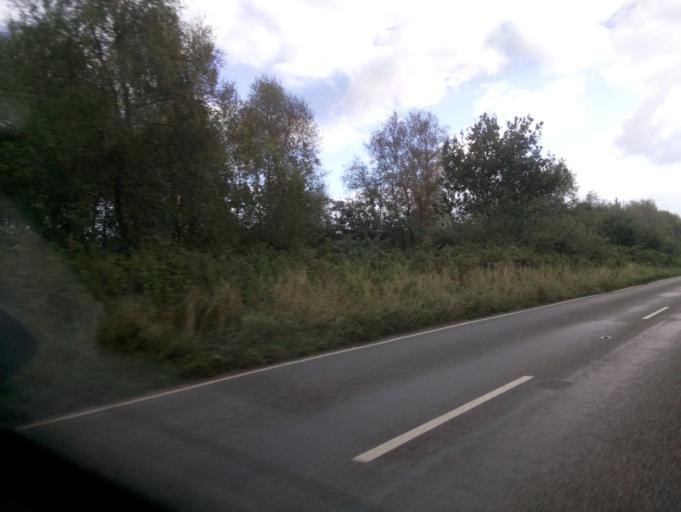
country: GB
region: England
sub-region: Devon
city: Honiton
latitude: 50.7698
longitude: -3.2116
